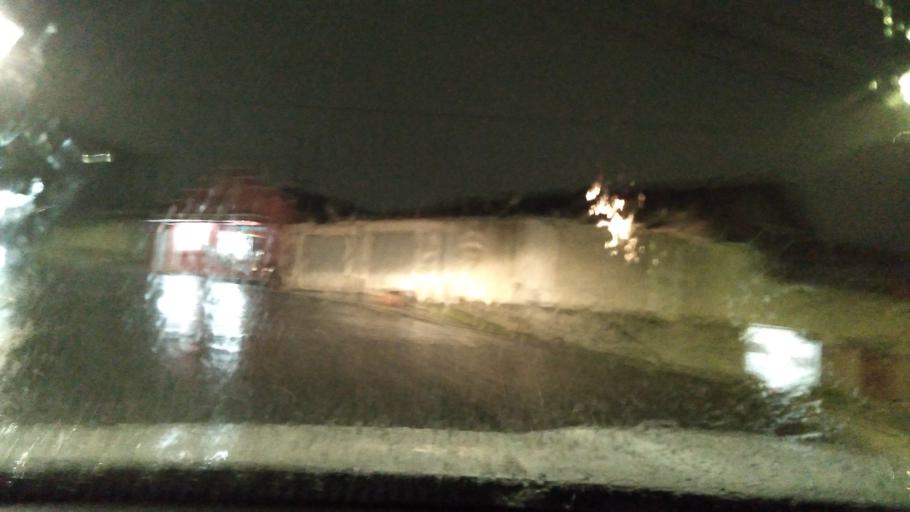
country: BR
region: Minas Gerais
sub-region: Belo Horizonte
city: Belo Horizonte
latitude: -19.8780
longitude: -43.9479
